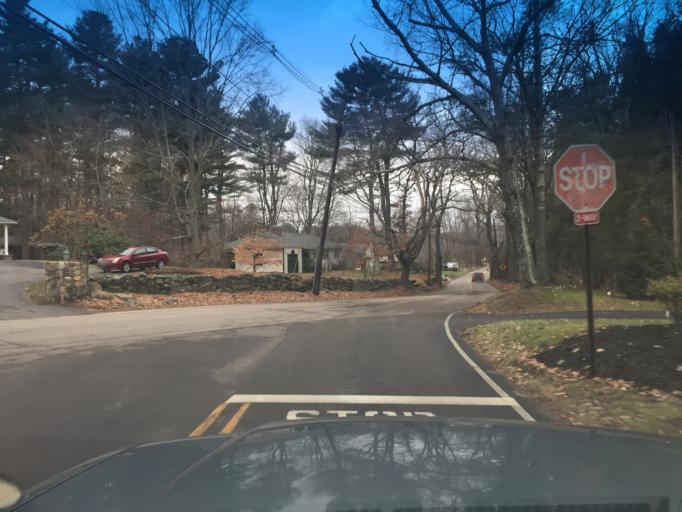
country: US
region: Massachusetts
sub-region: Norfolk County
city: Millis
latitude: 42.1769
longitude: -71.3675
